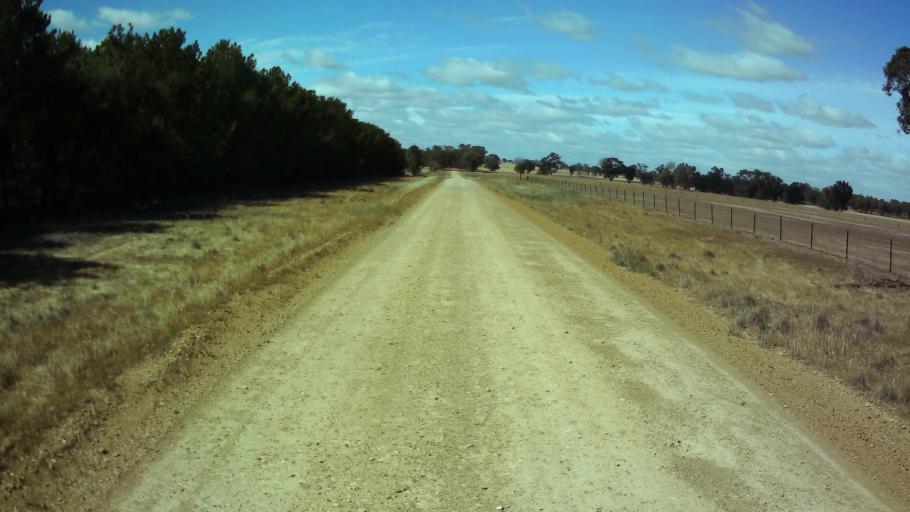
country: AU
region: New South Wales
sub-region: Weddin
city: Grenfell
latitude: -34.0586
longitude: 148.3125
